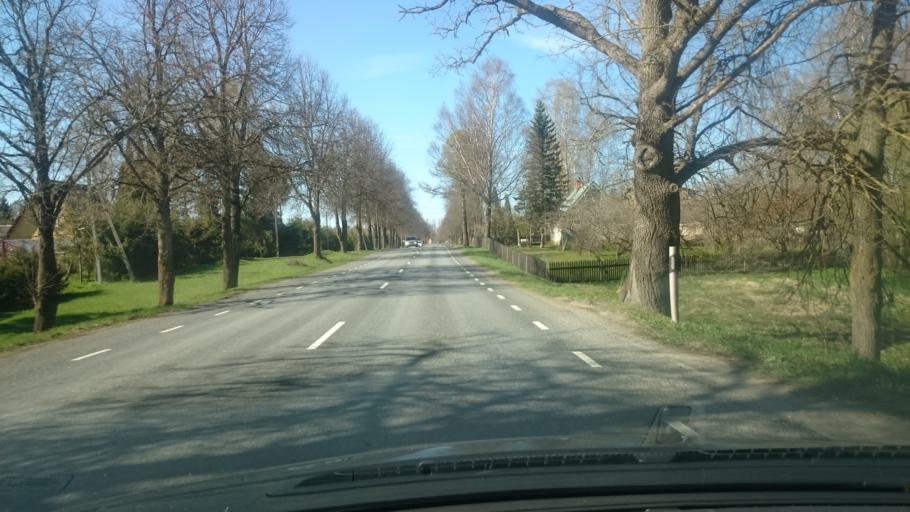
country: EE
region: Polvamaa
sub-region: Polva linn
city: Polva
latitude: 58.1999
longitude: 27.0775
